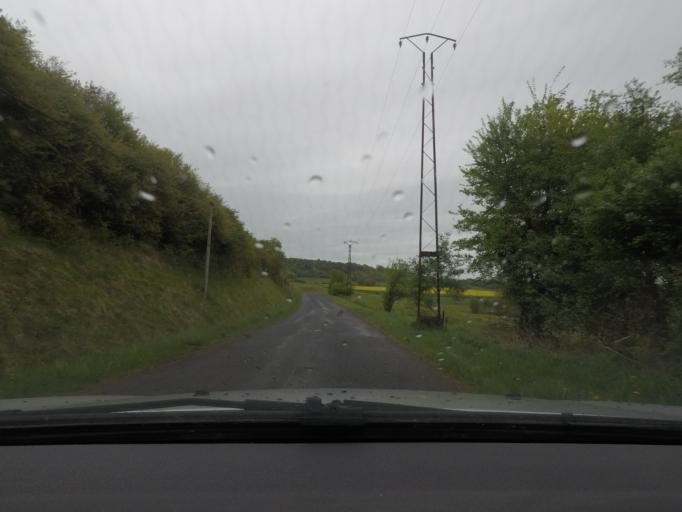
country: BE
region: Wallonia
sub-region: Province du Luxembourg
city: Rouvroy
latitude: 49.4973
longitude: 5.4347
